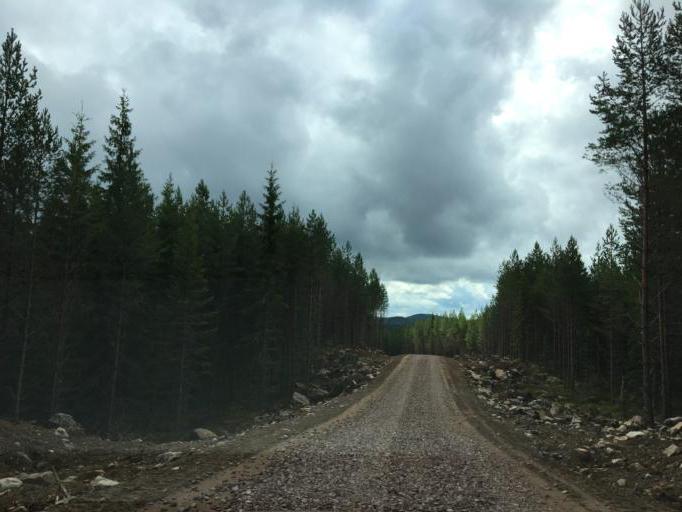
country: SE
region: OErebro
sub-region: Hallefors Kommun
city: Haellefors
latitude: 60.0782
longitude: 14.4731
